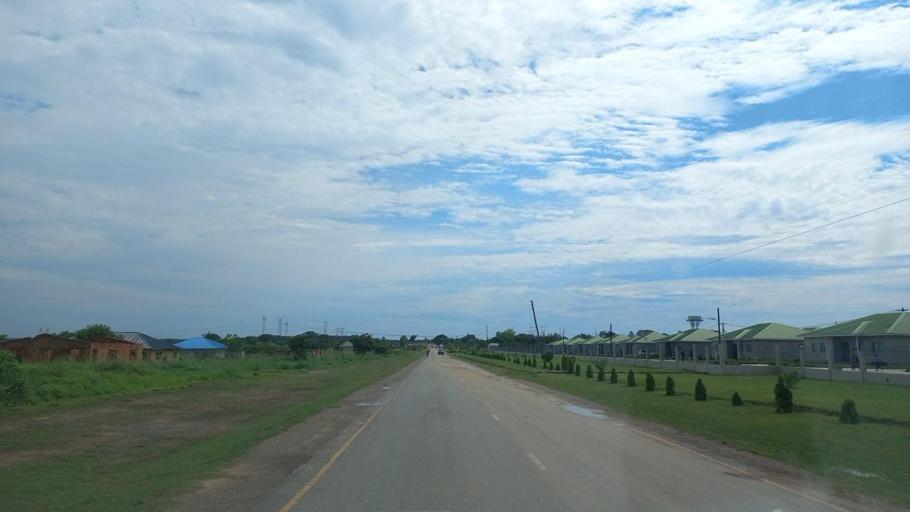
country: ZM
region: Copperbelt
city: Kitwe
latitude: -12.8724
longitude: 28.3358
